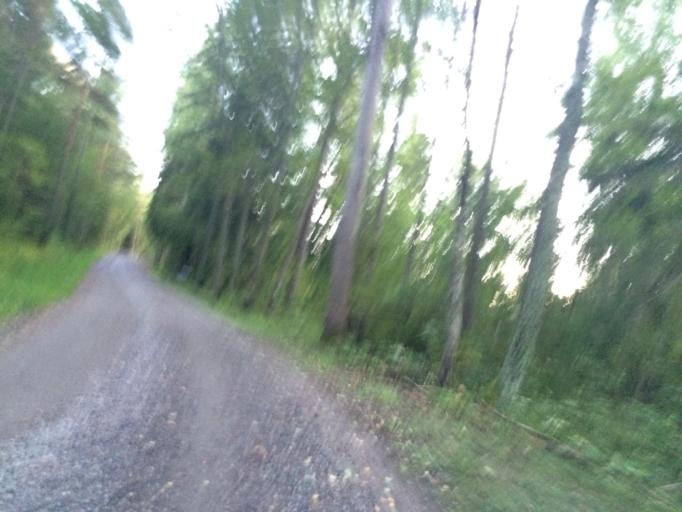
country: SE
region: Soedermanland
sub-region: Eskilstuna Kommun
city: Kvicksund
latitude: 59.4513
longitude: 16.3563
